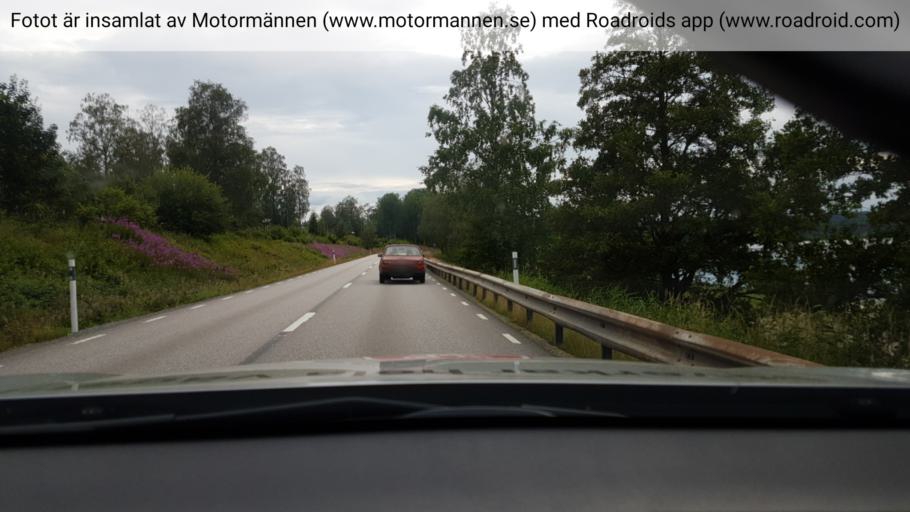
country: SE
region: Vaestra Goetaland
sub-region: Bengtsfors Kommun
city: Dals Langed
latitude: 58.8743
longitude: 12.2097
